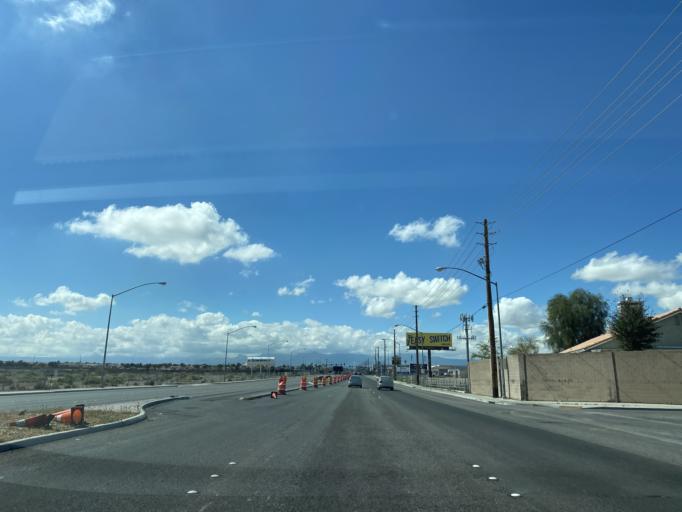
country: US
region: Nevada
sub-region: Clark County
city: North Las Vegas
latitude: 36.2397
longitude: -115.1295
